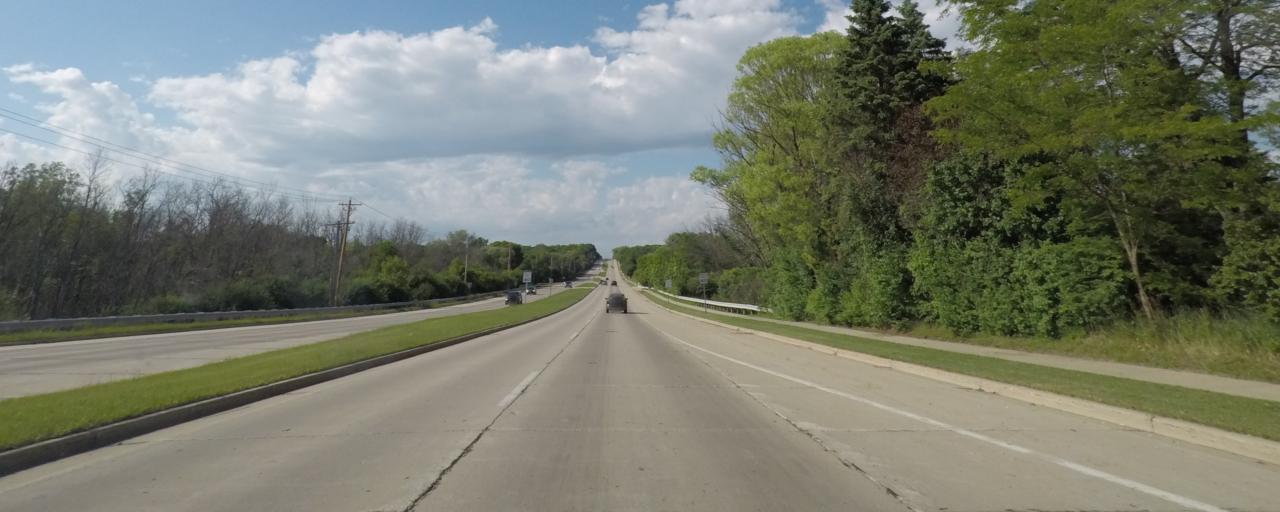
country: US
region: Wisconsin
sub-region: Milwaukee County
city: Greendale
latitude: 42.9260
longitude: -88.0088
